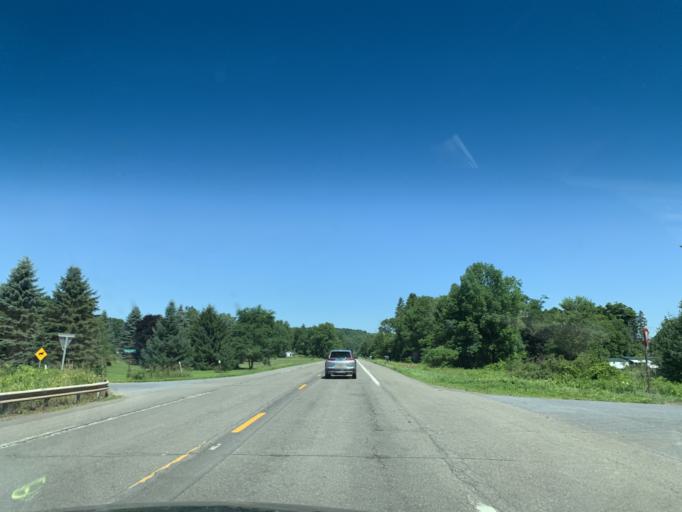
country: US
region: New York
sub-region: Delaware County
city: Sidney
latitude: 42.4558
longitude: -75.3959
